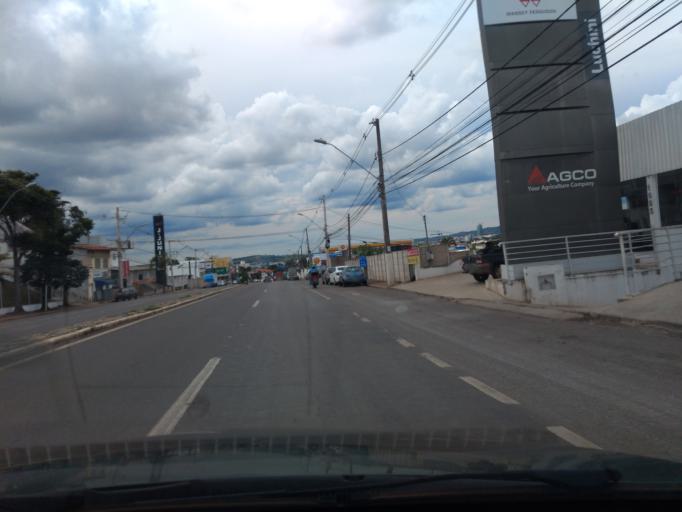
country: BR
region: Minas Gerais
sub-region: Varginha
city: Varginha
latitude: -21.5828
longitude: -45.4405
